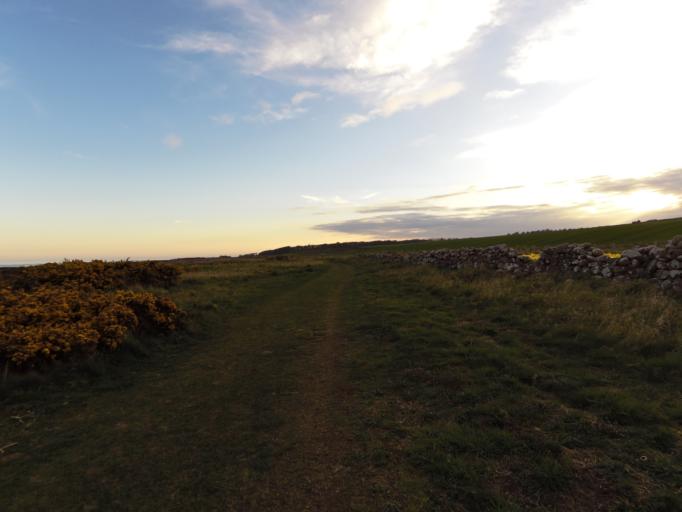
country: GB
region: Scotland
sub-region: Aberdeenshire
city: Inverbervie
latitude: 56.8168
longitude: -2.3001
